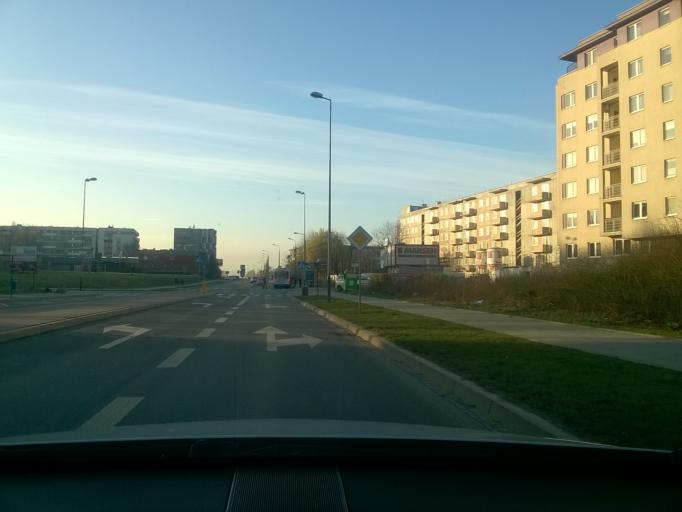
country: PL
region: Lesser Poland Voivodeship
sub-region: Krakow
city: Krakow
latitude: 50.0936
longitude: 19.9877
